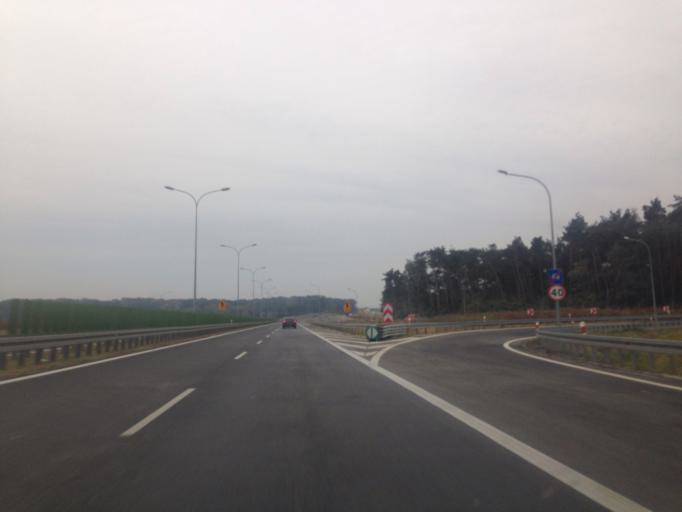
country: PL
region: Greater Poland Voivodeship
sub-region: Powiat poznanski
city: Kostrzyn
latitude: 52.4136
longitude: 17.2872
